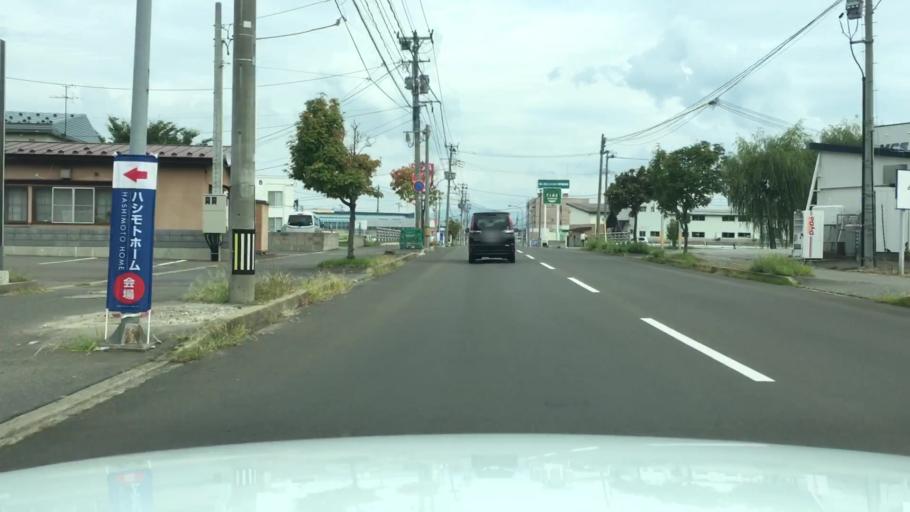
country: JP
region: Aomori
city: Hirosaki
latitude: 40.6160
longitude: 140.4878
